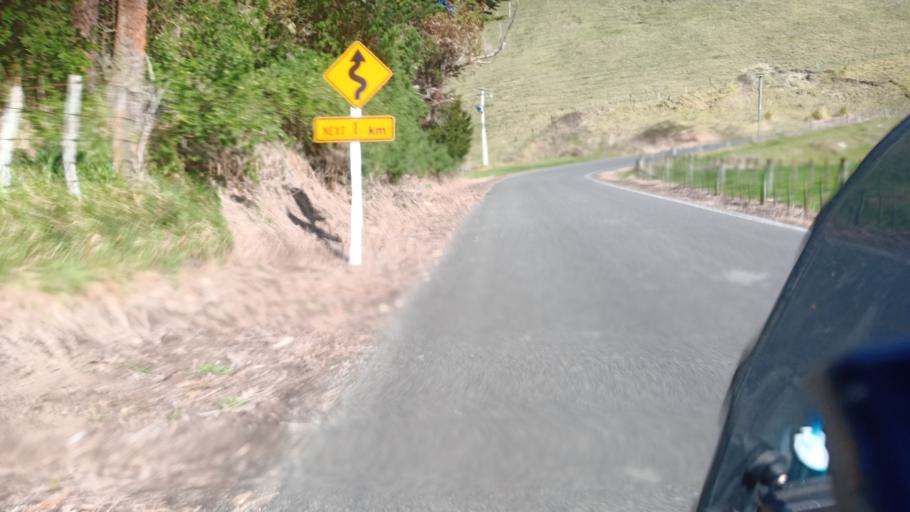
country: NZ
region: Gisborne
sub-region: Gisborne District
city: Gisborne
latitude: -39.0979
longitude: 177.9630
